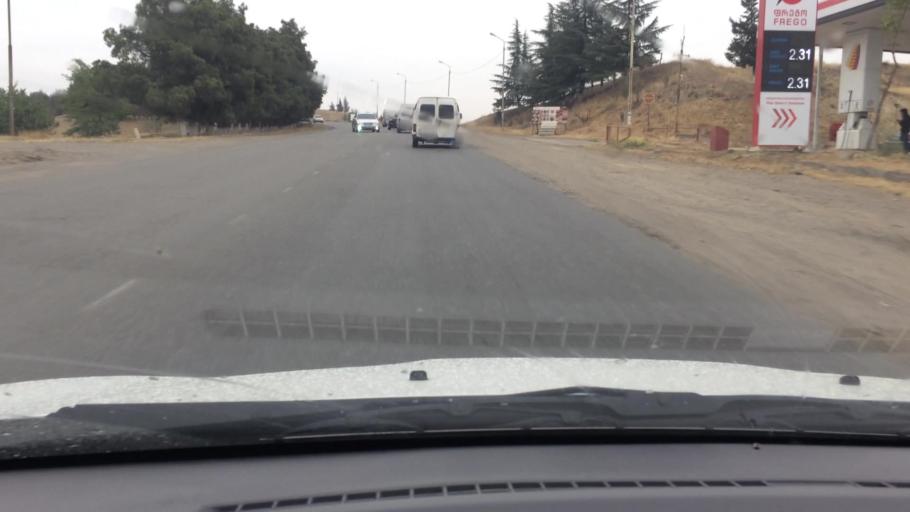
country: GE
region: Kvemo Kartli
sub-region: Marneuli
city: Marneuli
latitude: 41.4982
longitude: 44.8030
